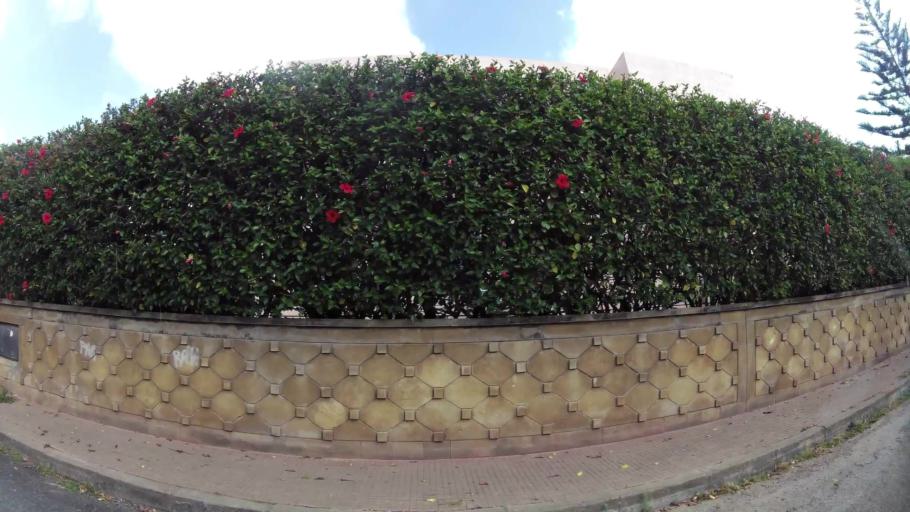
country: MA
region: Rabat-Sale-Zemmour-Zaer
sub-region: Skhirate-Temara
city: Temara
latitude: 33.9570
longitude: -6.8635
